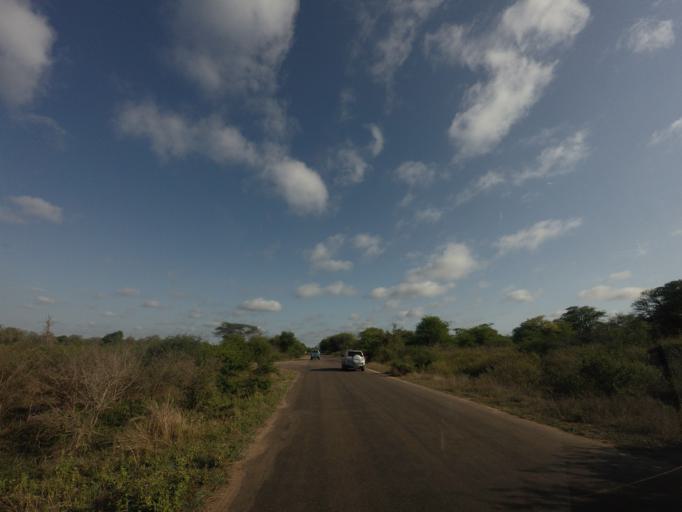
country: ZA
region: Mpumalanga
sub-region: Ehlanzeni District
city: Komatipoort
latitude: -25.2572
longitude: 31.8471
